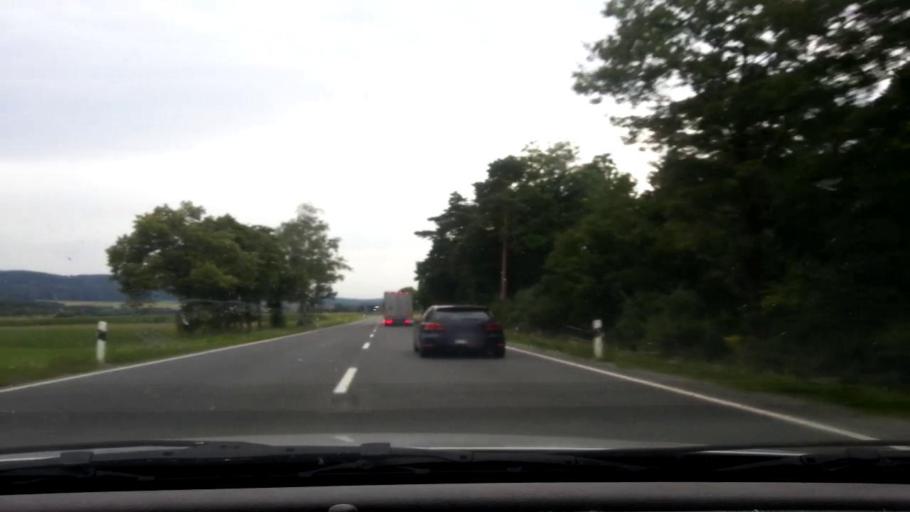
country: DE
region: Bavaria
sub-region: Upper Franconia
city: Emtmannsberg
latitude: 49.9052
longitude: 11.6826
